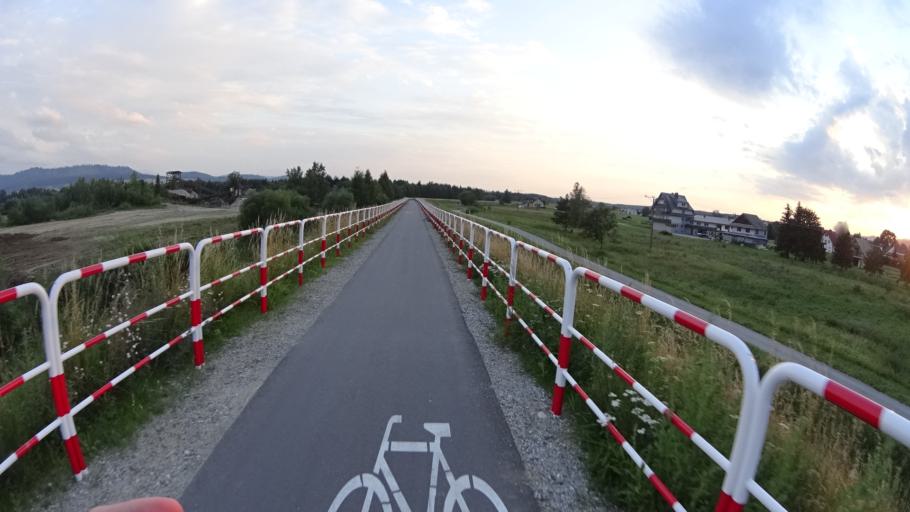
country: PL
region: Lesser Poland Voivodeship
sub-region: Powiat nowotarski
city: Frydman
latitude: 49.4647
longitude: 20.2180
